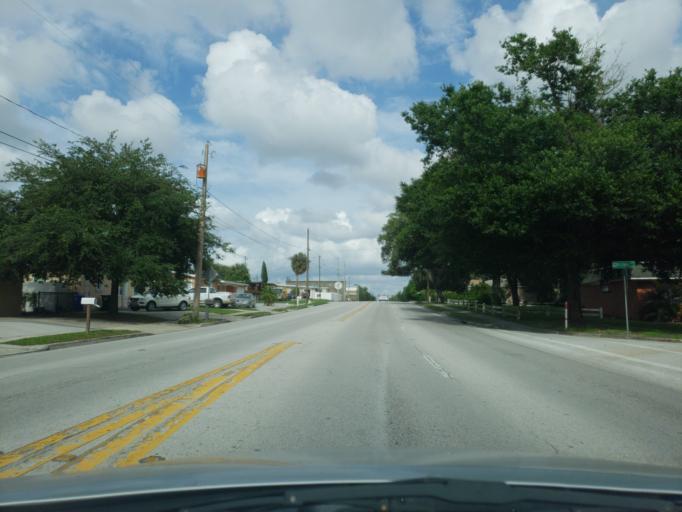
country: US
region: Florida
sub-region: Hillsborough County
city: Egypt Lake-Leto
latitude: 28.0107
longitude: -82.4876
